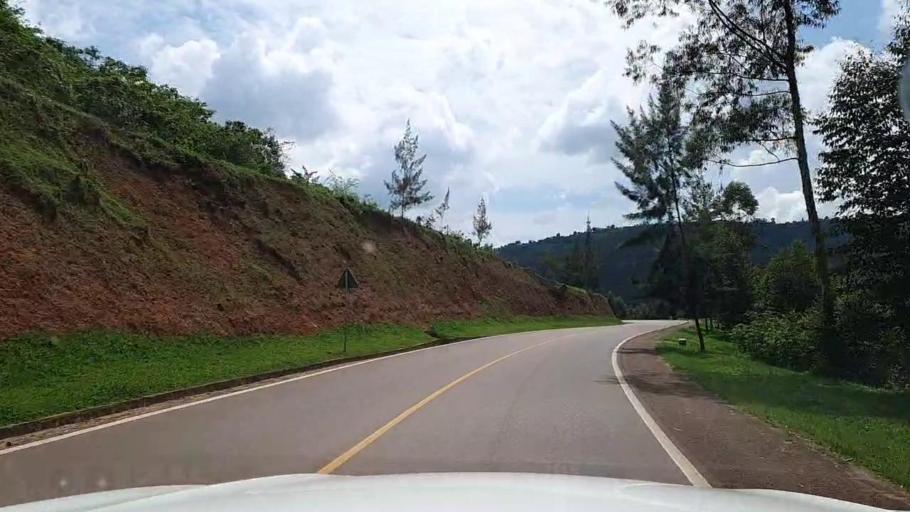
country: RW
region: Kigali
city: Kigali
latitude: -1.8154
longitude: 30.1087
